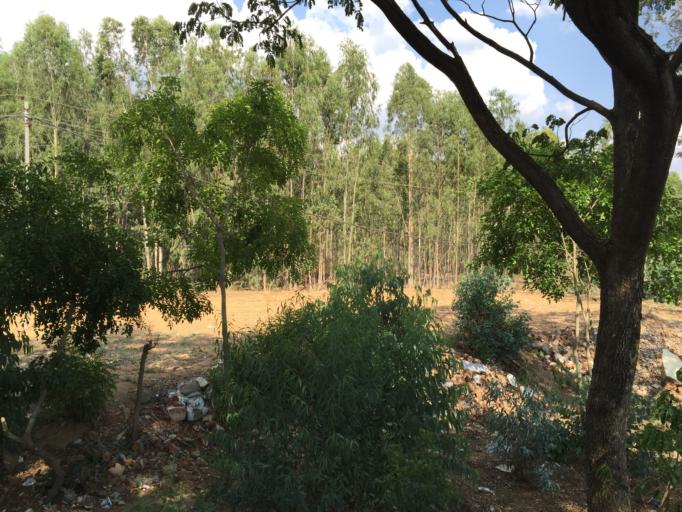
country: IN
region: Karnataka
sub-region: Chikkaballapur
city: Chik Ballapur
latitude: 13.3446
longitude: 77.6878
